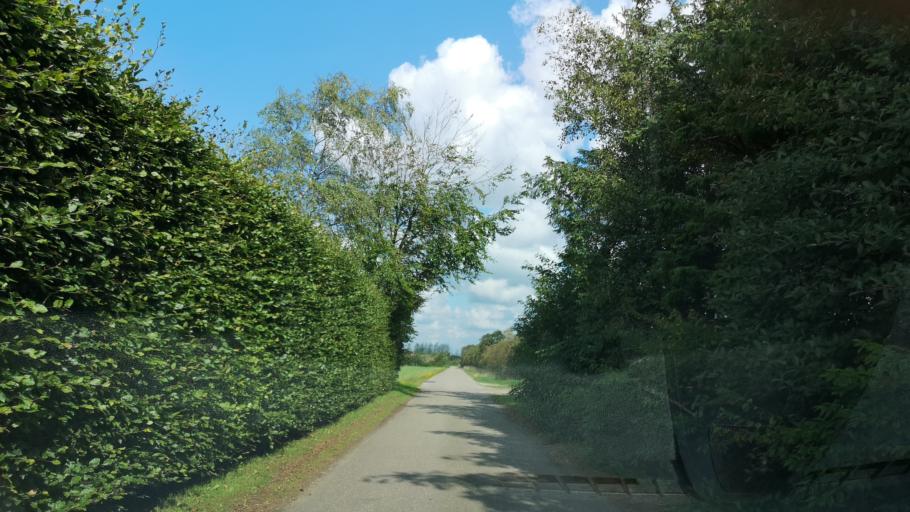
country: DK
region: Central Jutland
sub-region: Ringkobing-Skjern Kommune
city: Skjern
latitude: 55.9346
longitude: 8.4607
